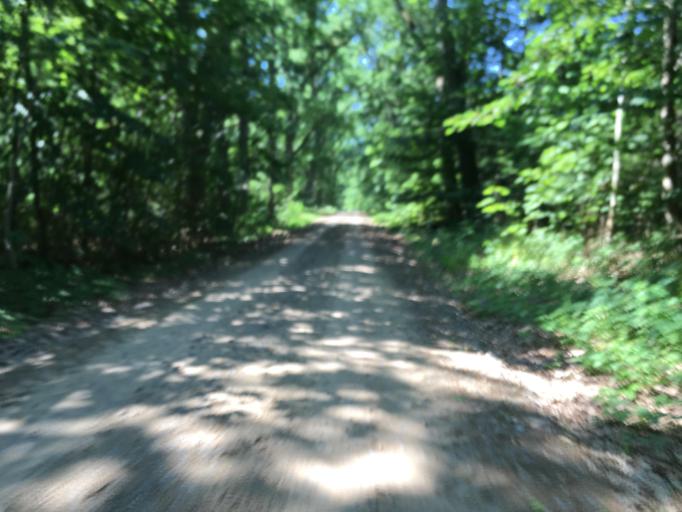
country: DE
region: Brandenburg
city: Marienwerder
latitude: 52.9162
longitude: 13.6449
